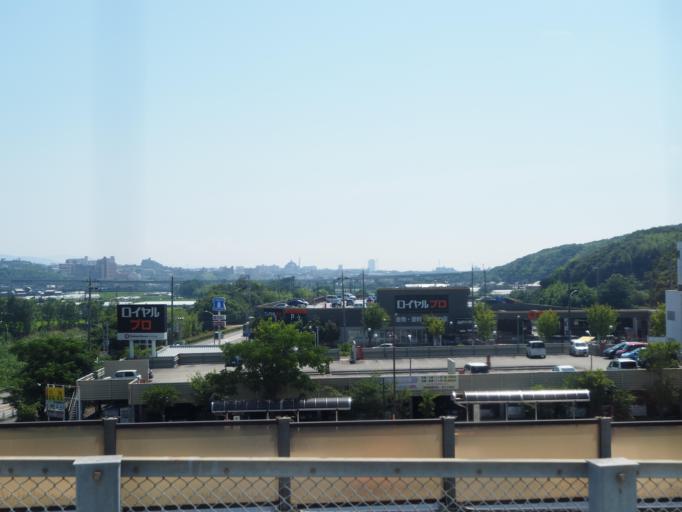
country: JP
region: Hyogo
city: Akashi
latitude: 34.6876
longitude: 135.0416
